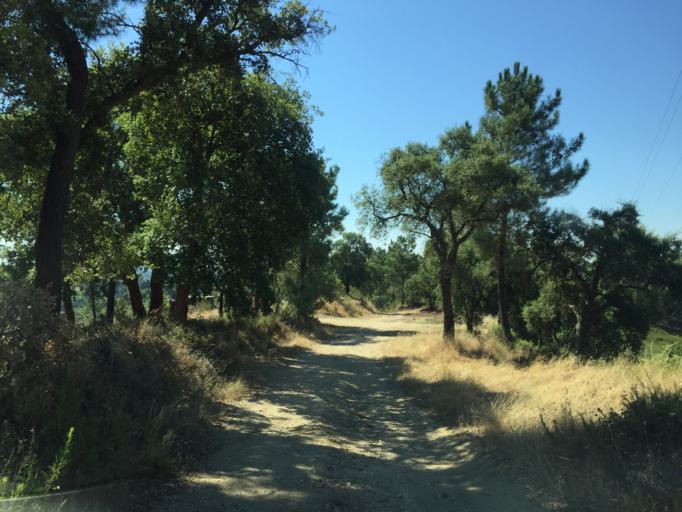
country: PT
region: Santarem
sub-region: Ferreira do Zezere
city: Ferreira do Zezere
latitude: 39.5839
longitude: -8.2766
